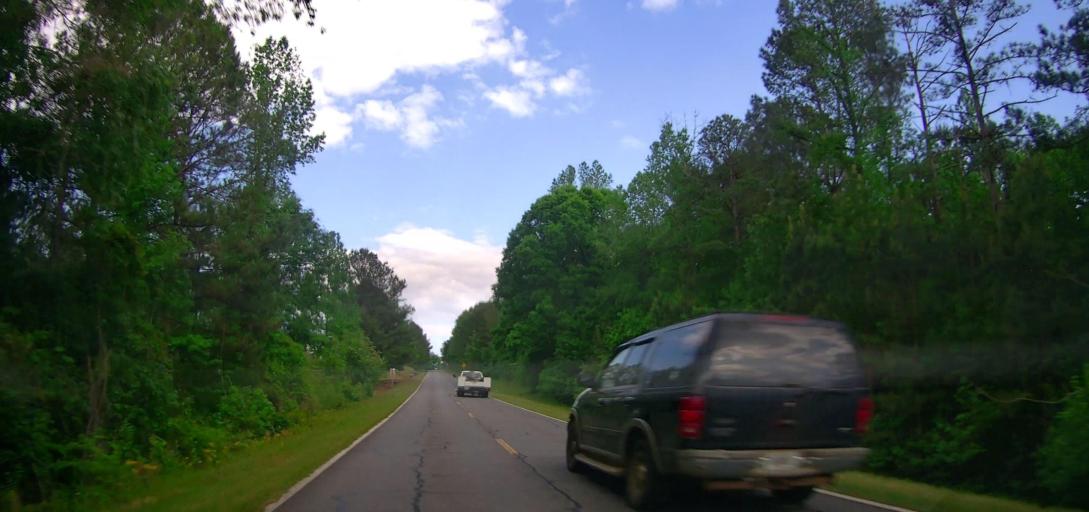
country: US
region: Georgia
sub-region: Baldwin County
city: Hardwick
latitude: 33.0628
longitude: -83.1460
